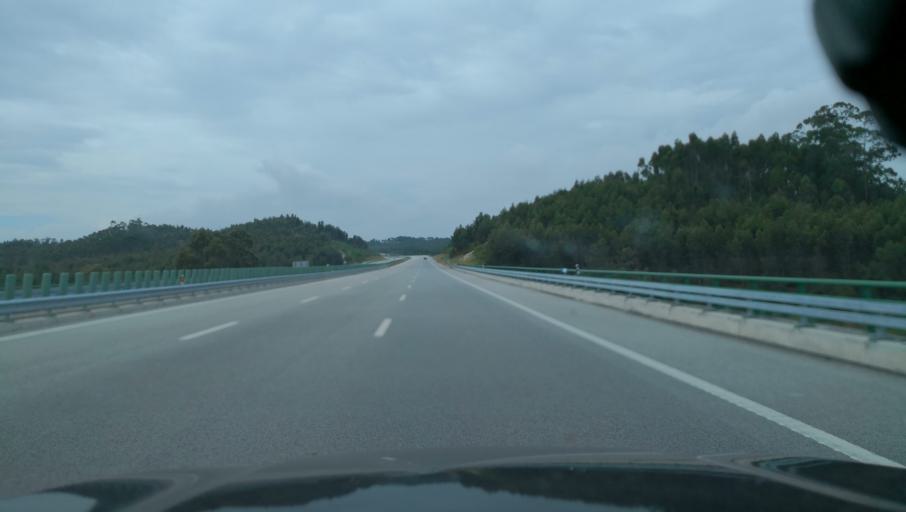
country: PT
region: Coimbra
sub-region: Figueira da Foz
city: Alhadas
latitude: 40.1273
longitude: -8.7455
